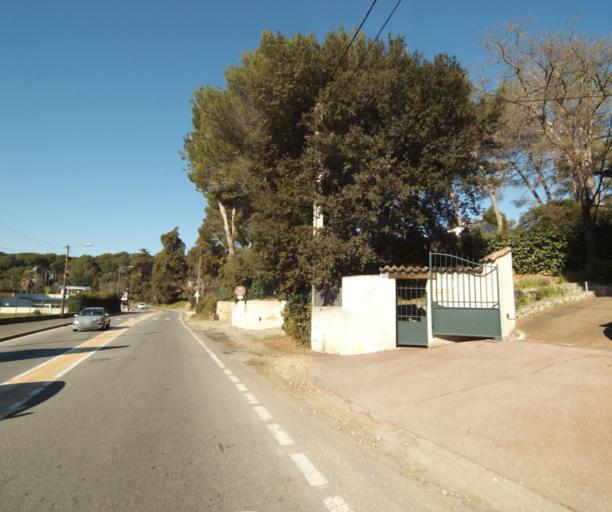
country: FR
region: Provence-Alpes-Cote d'Azur
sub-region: Departement des Alpes-Maritimes
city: Biot
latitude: 43.6008
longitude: 7.0985
